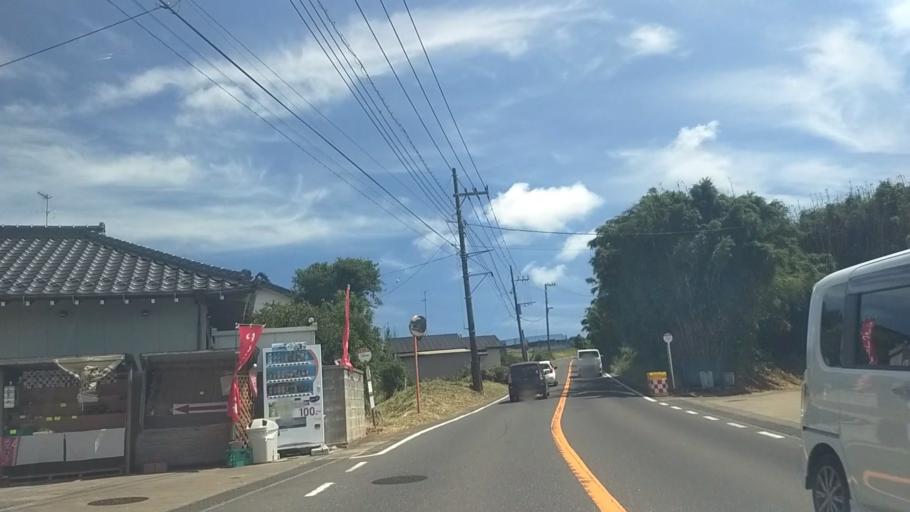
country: JP
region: Kanagawa
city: Miura
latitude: 35.2007
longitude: 139.6505
